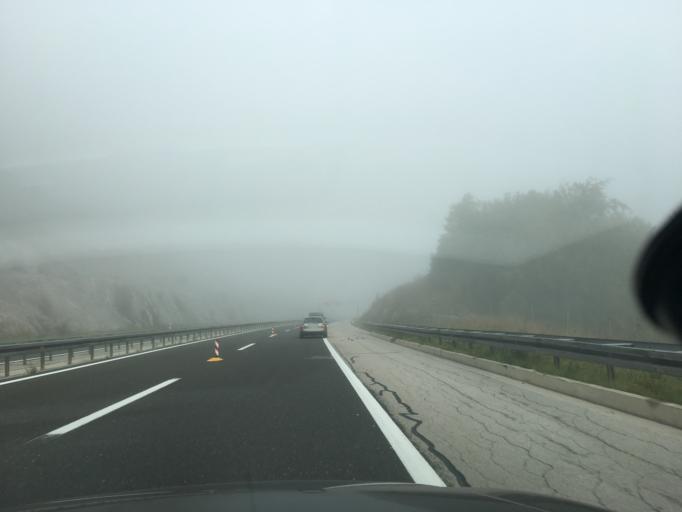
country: HR
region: Licko-Senjska
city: Otocac
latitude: 44.8587
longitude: 15.2163
